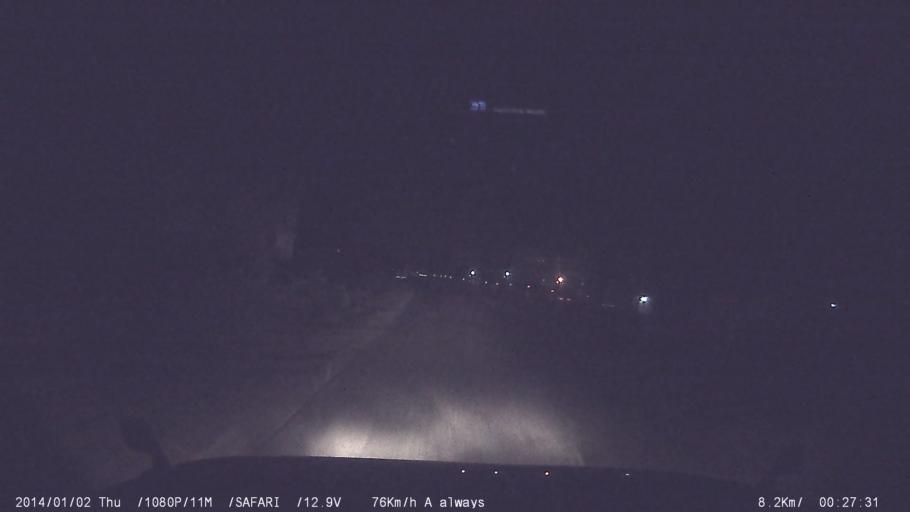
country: IN
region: Kerala
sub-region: Palakkad district
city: Chittur
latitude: 10.7977
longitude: 76.7634
